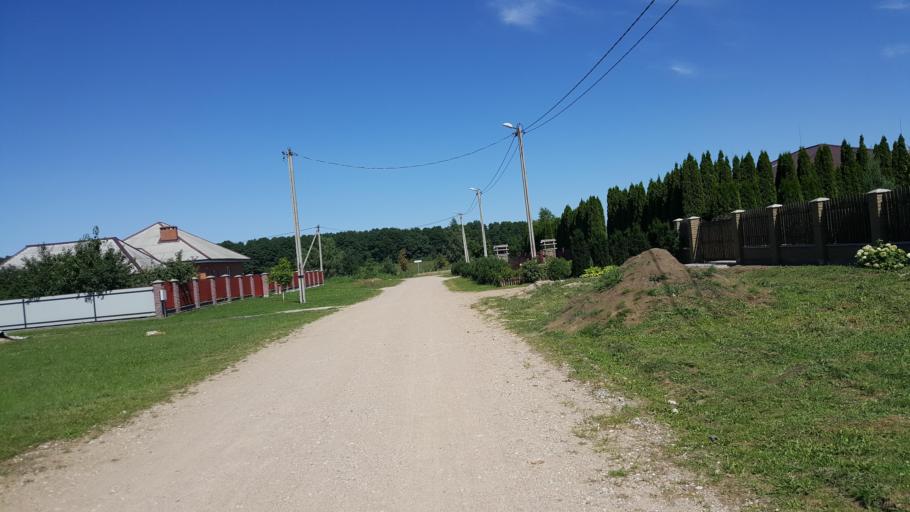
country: BY
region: Brest
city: Charnawchytsy
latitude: 52.2125
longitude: 23.7279
